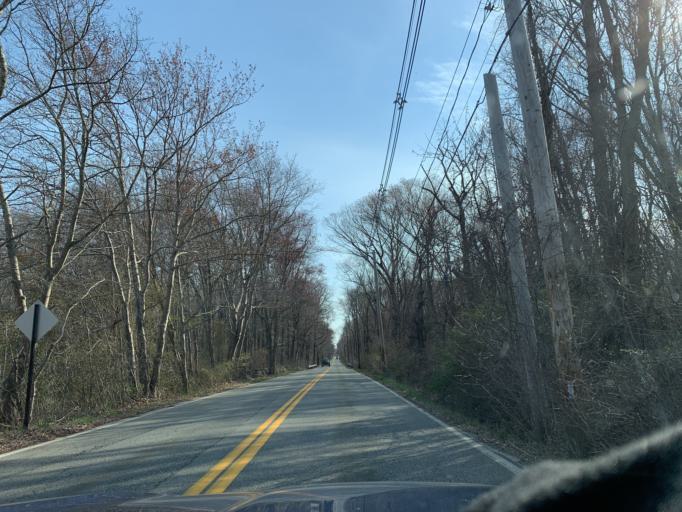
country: US
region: Rhode Island
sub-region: Kent County
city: West Warwick
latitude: 41.7478
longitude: -71.5269
